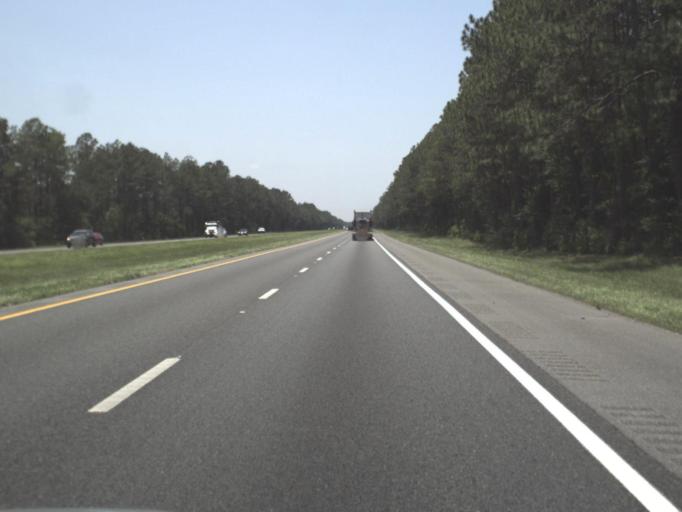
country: US
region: Florida
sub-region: Baker County
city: Macclenny
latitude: 30.2474
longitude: -82.2291
